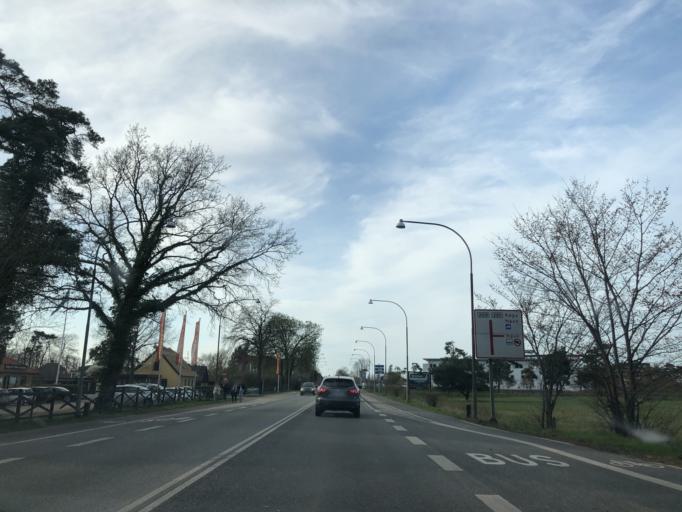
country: DK
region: Zealand
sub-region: Koge Kommune
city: Koge
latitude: 55.4453
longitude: 12.1934
